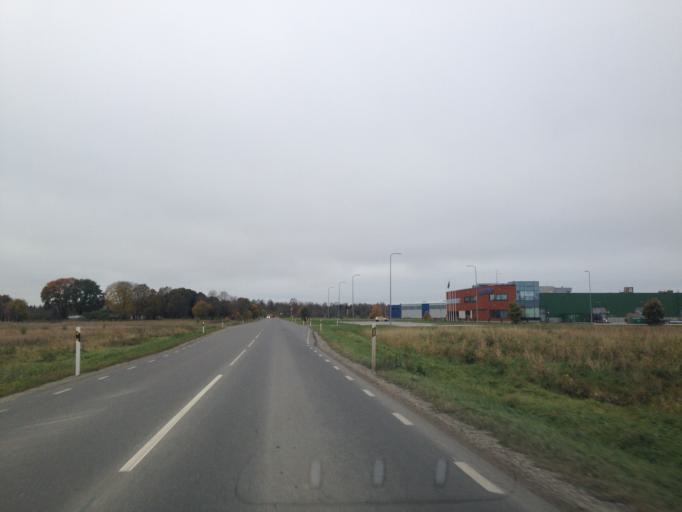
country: EE
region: Harju
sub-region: Harku vald
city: Tabasalu
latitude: 59.4181
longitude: 24.5427
